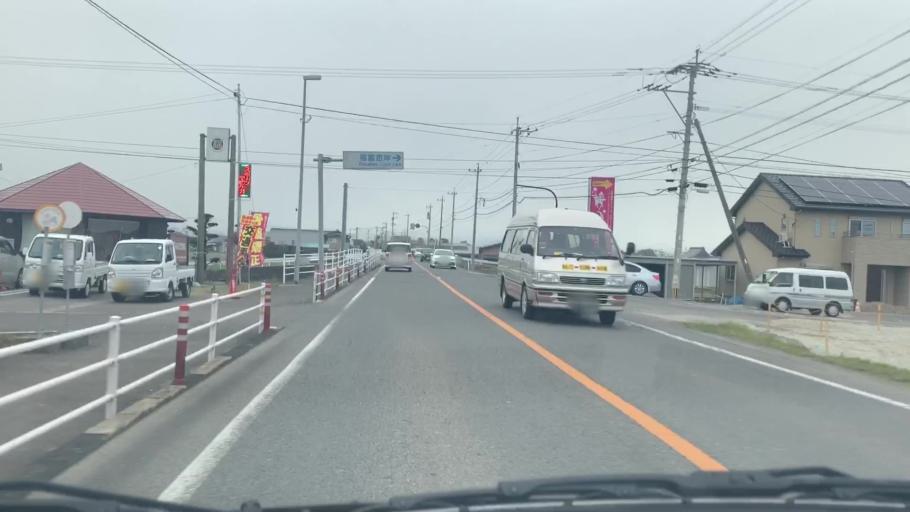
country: JP
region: Saga Prefecture
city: Saga-shi
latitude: 33.1930
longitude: 130.1929
